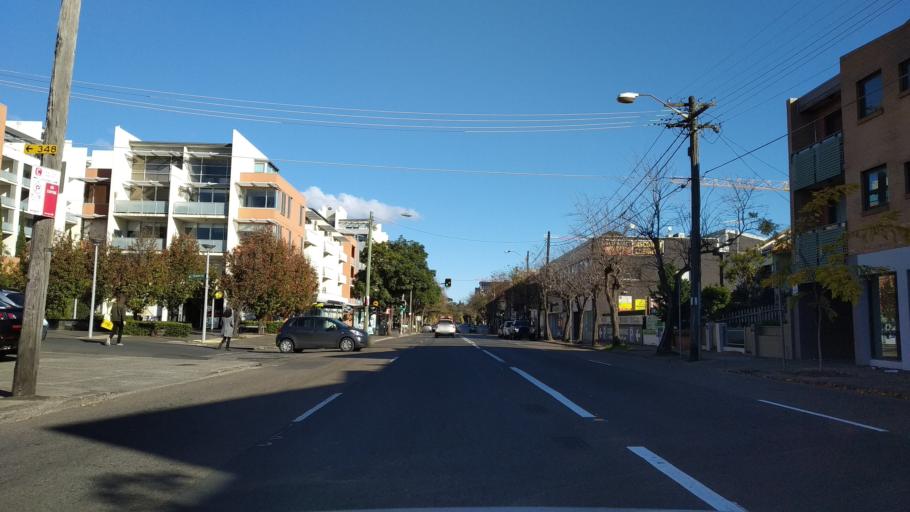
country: AU
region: New South Wales
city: Alexandria
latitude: -33.9138
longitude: 151.2011
